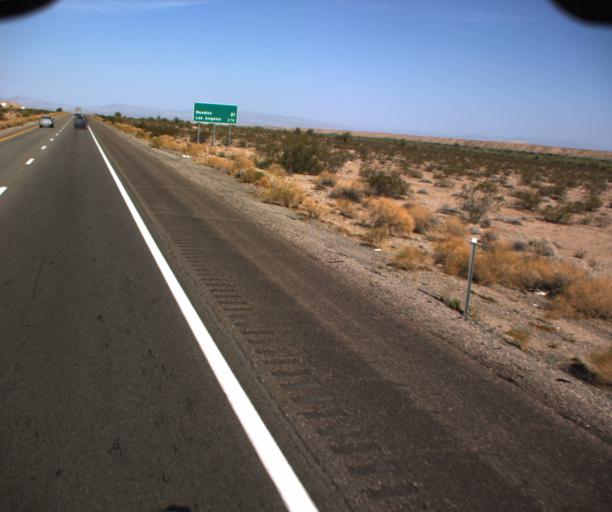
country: US
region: Arizona
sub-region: Mohave County
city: Desert Hills
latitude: 34.7293
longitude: -114.3322
